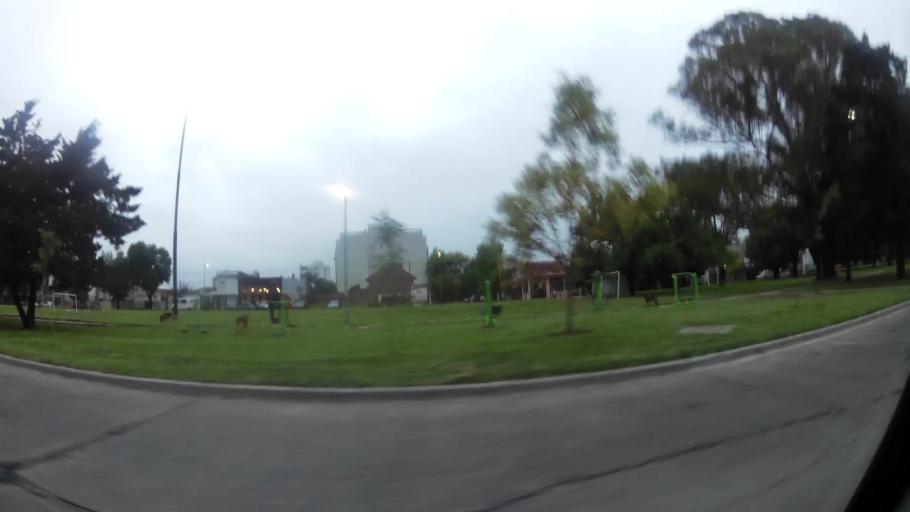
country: AR
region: Buenos Aires
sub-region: Partido de La Plata
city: La Plata
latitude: -34.9095
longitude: -57.9797
